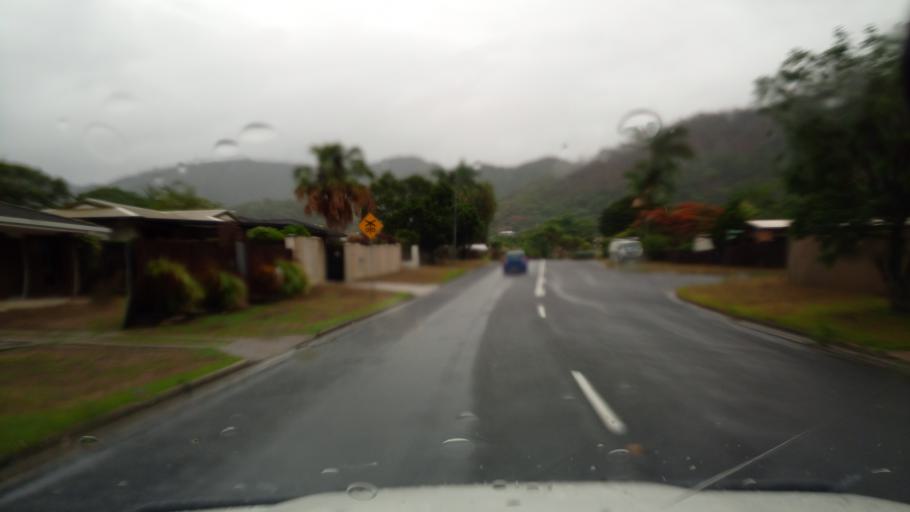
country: AU
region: Queensland
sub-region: Cairns
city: Woree
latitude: -16.9373
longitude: 145.7327
